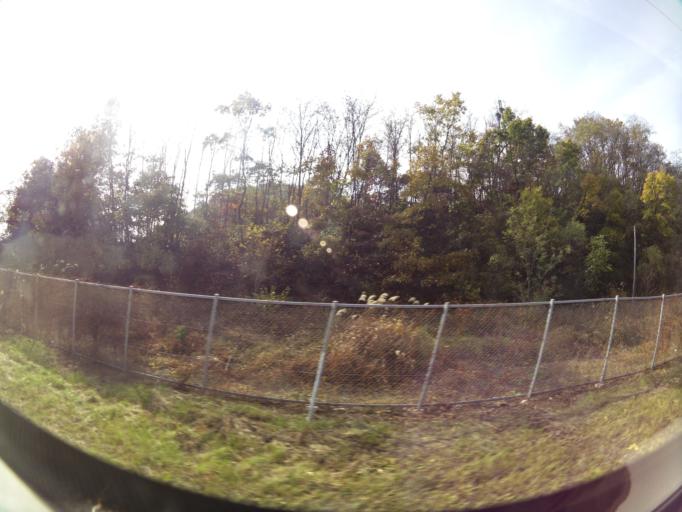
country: KR
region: Chungcheongbuk-do
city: Cheongju-si
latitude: 36.6347
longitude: 127.2881
